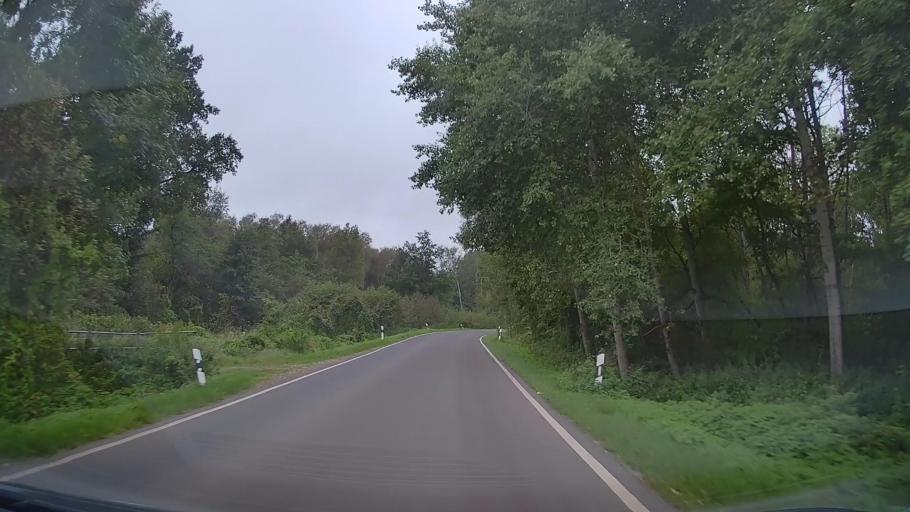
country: DE
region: Mecklenburg-Vorpommern
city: Dummerstorf
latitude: 53.9764
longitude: 12.2625
